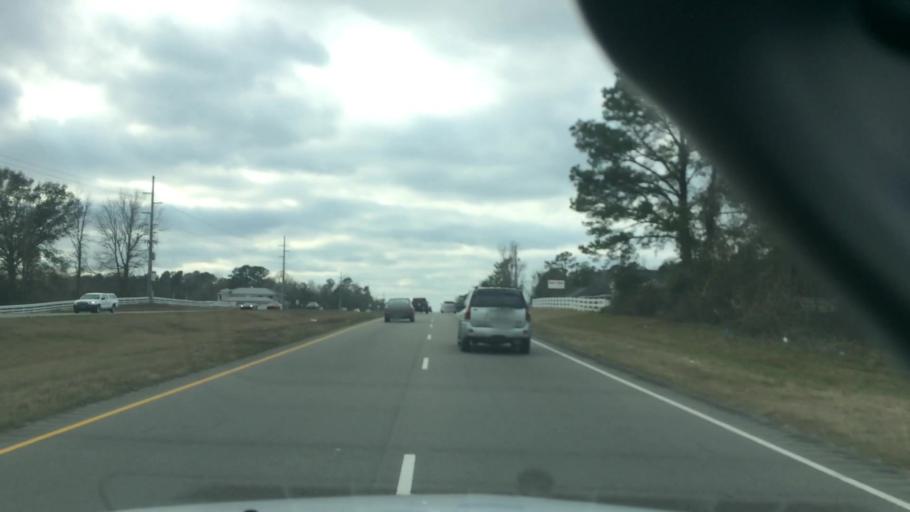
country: US
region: North Carolina
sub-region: Brunswick County
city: Shallotte
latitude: 34.0119
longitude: -78.2892
